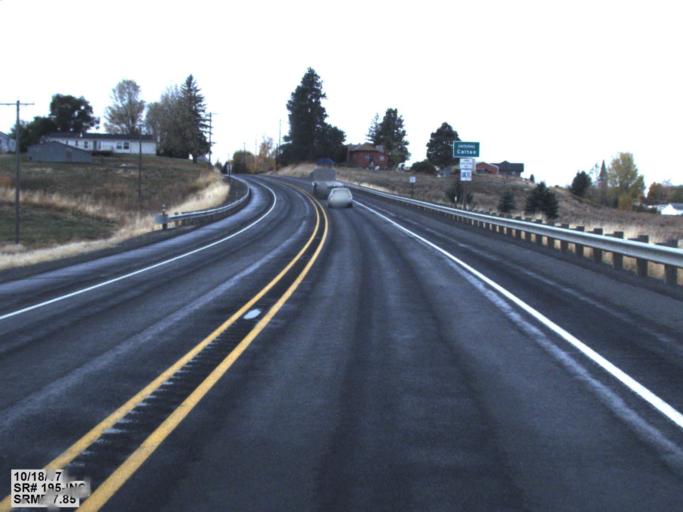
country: US
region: Washington
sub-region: Asotin County
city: Clarkston
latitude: 46.5677
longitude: -117.1208
